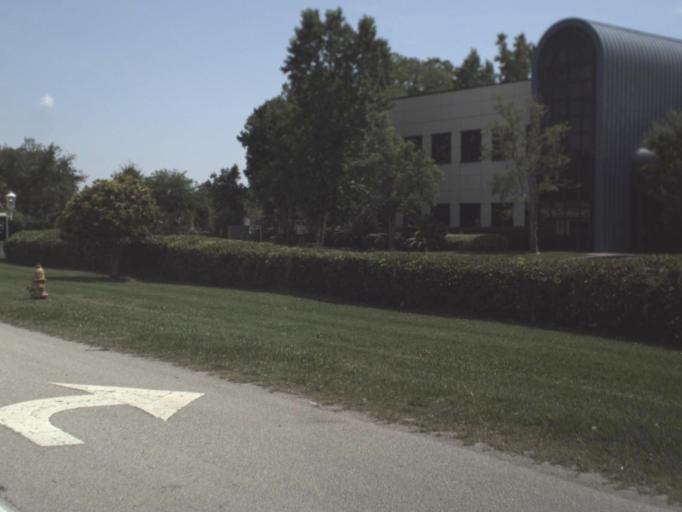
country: US
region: Florida
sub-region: Duval County
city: Jacksonville
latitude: 30.2831
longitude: -81.6305
